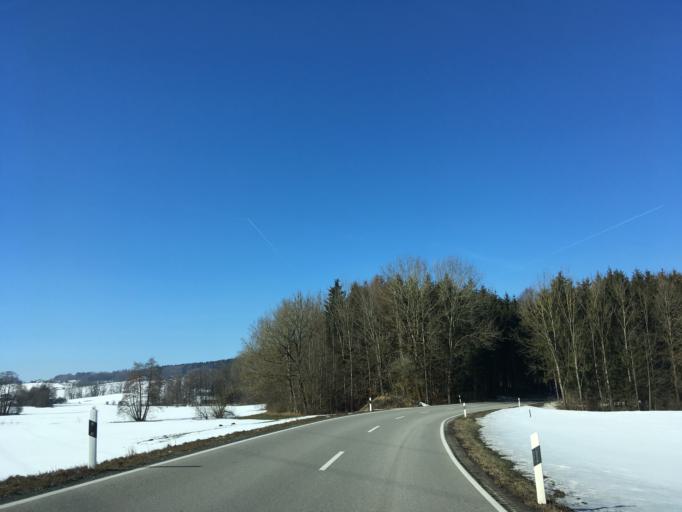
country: DE
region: Bavaria
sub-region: Upper Bavaria
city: Albaching
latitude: 48.1171
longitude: 12.0925
